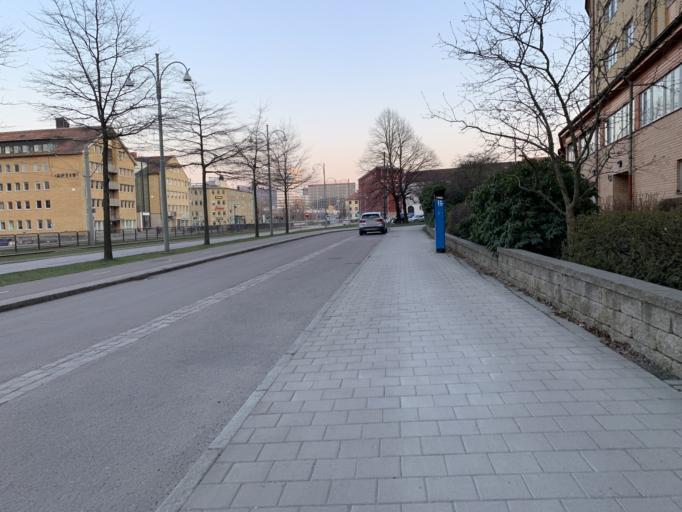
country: SE
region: Vaestra Goetaland
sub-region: Goteborg
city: Goeteborg
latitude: 57.6882
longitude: 11.9954
